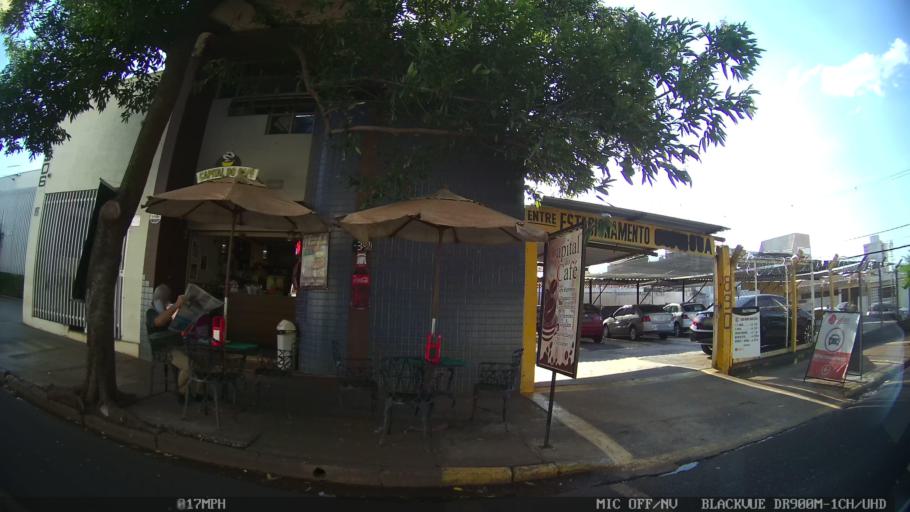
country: BR
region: Sao Paulo
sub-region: Ribeirao Preto
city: Ribeirao Preto
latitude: -21.1879
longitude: -47.8057
